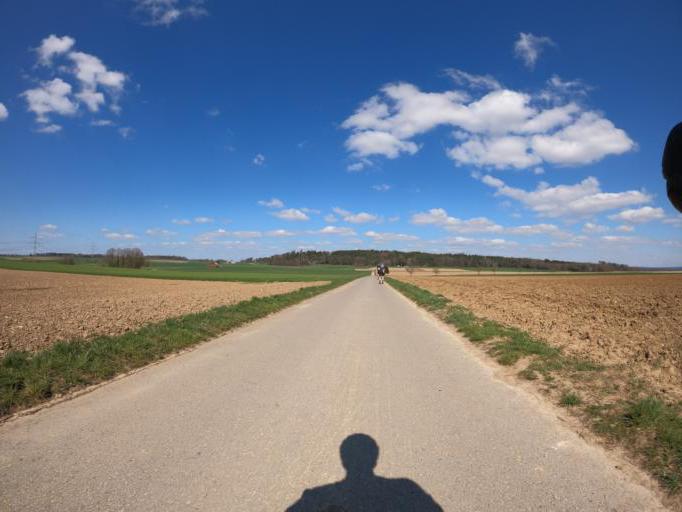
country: DE
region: Baden-Wuerttemberg
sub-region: Regierungsbezirk Stuttgart
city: Bondorf
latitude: 48.4764
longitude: 8.8649
